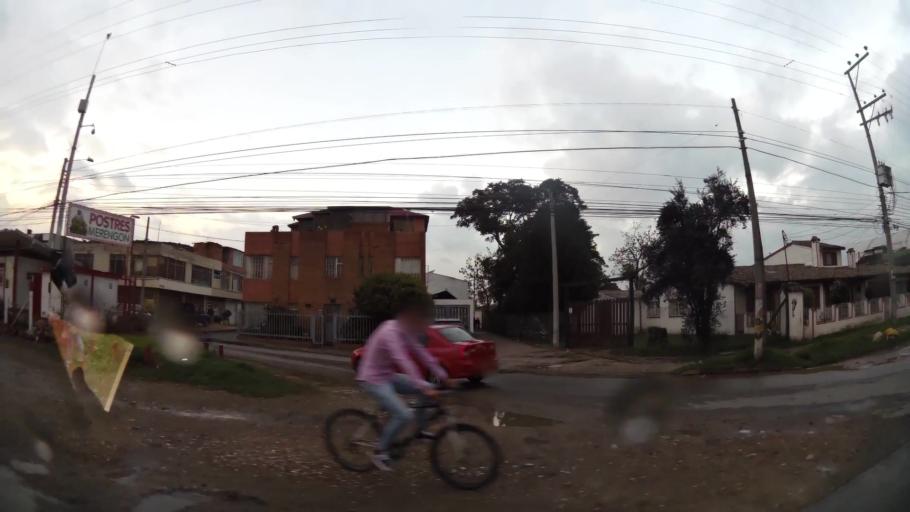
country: CO
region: Cundinamarca
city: Chia
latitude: 4.8517
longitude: -74.0614
